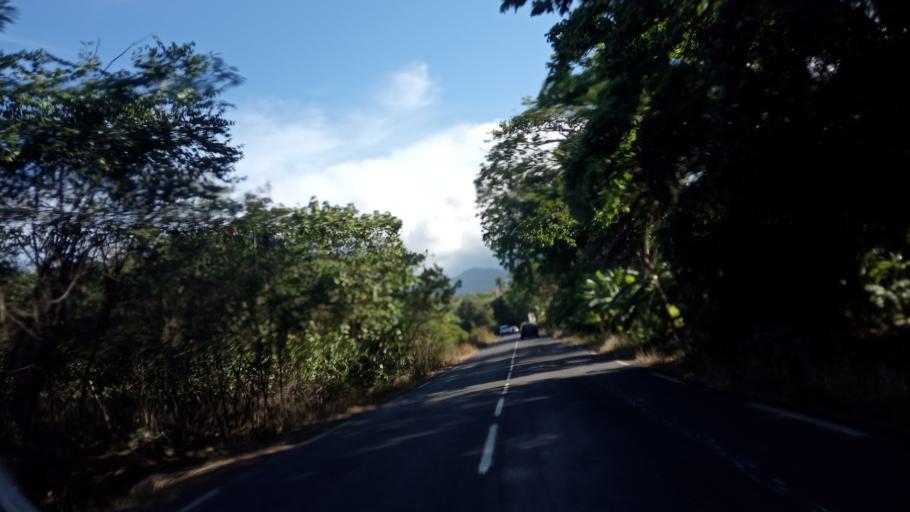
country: YT
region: Dembeni
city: Dembeni
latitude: -12.8260
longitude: 45.1938
